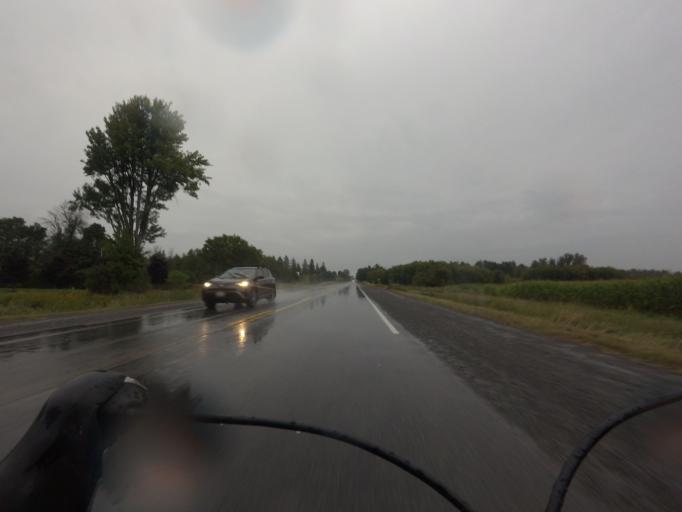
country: CA
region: Ontario
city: Bells Corners
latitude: 45.1787
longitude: -75.7189
